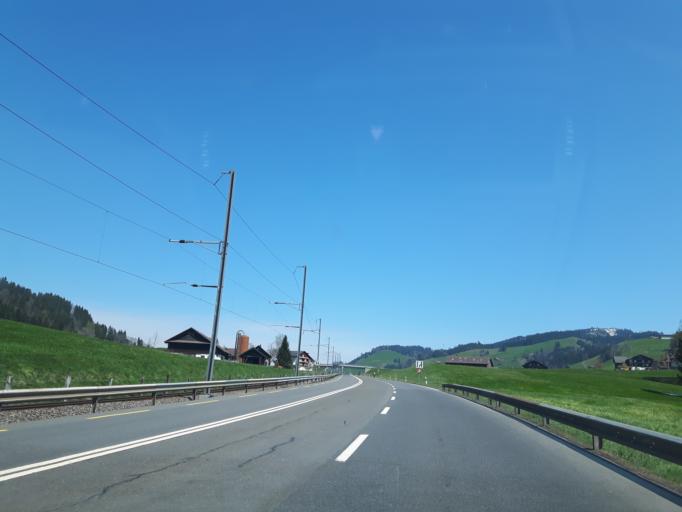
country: CH
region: Schwyz
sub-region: Bezirk Schwyz
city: Rothenthurm
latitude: 47.0896
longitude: 8.6662
